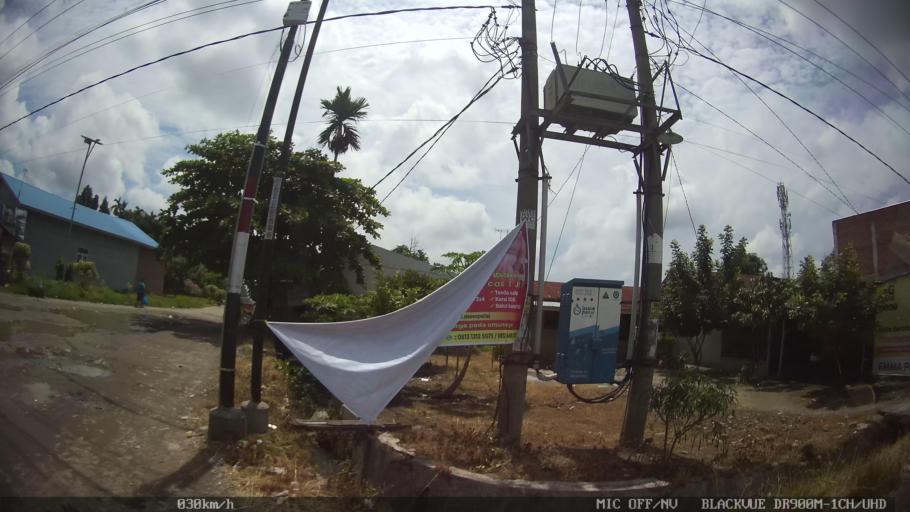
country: ID
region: North Sumatra
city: Medan
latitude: 3.6147
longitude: 98.7626
